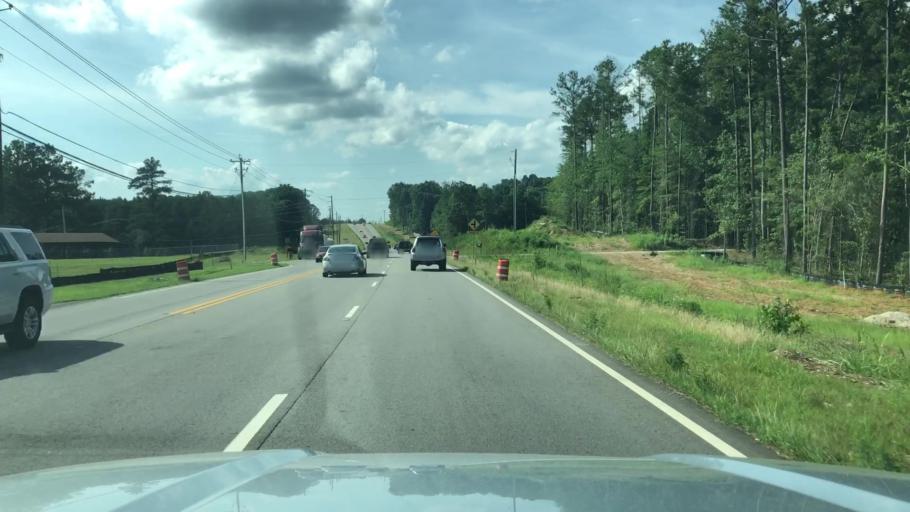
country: US
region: Georgia
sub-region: Douglas County
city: Douglasville
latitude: 33.7925
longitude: -84.7529
